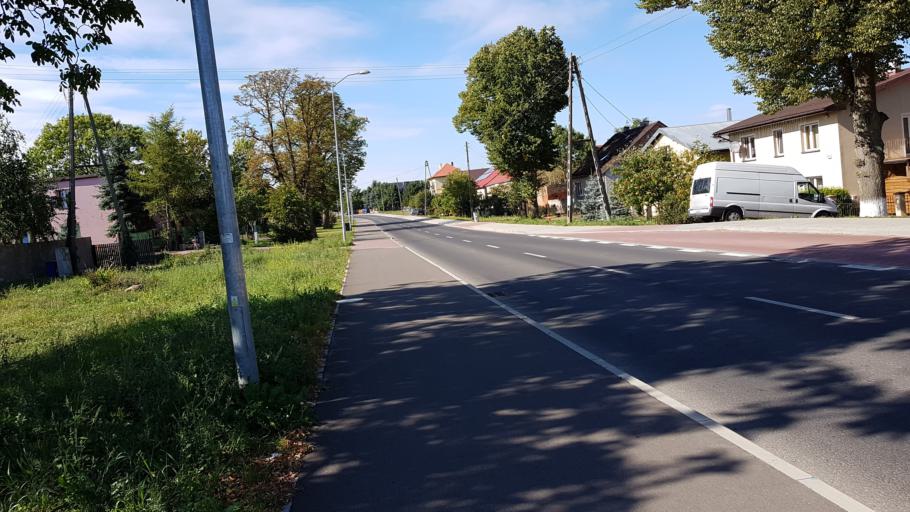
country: PL
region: West Pomeranian Voivodeship
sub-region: Powiat policki
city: Przeclaw
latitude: 53.3505
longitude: 14.4746
